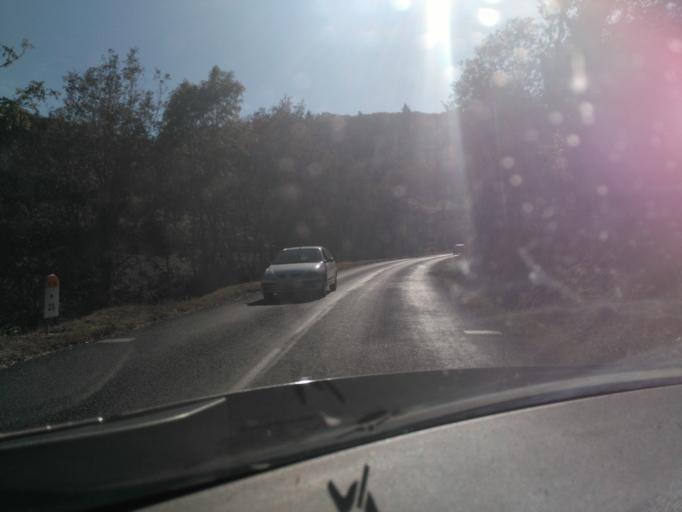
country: FR
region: Rhone-Alpes
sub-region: Departement du Rhone
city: Tarare
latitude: 45.8818
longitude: 4.4271
